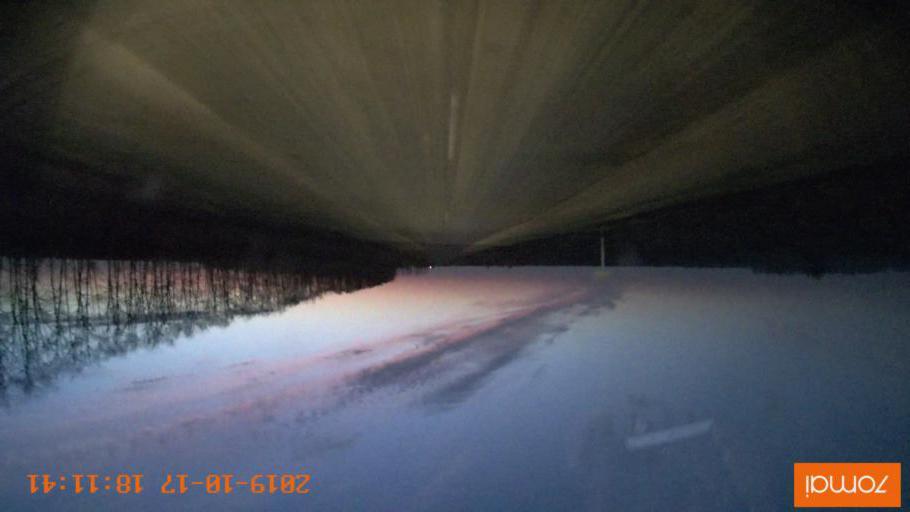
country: RU
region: Tula
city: Kurkino
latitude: 53.4143
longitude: 38.6244
